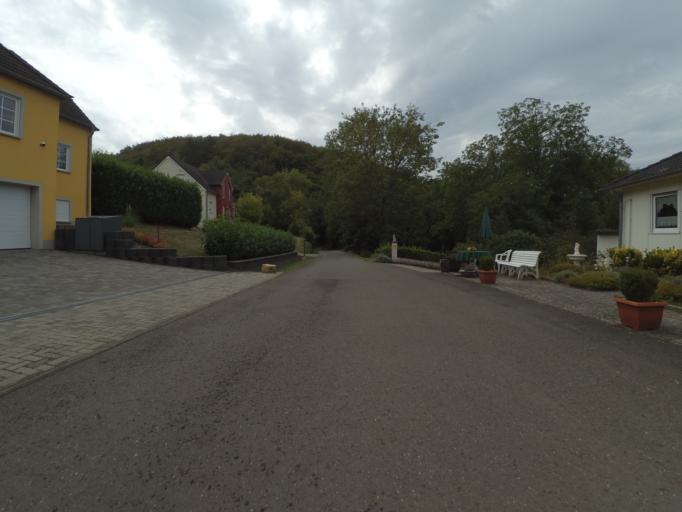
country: DE
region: Rheinland-Pfalz
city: Wincheringen
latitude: 49.6217
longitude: 6.4292
